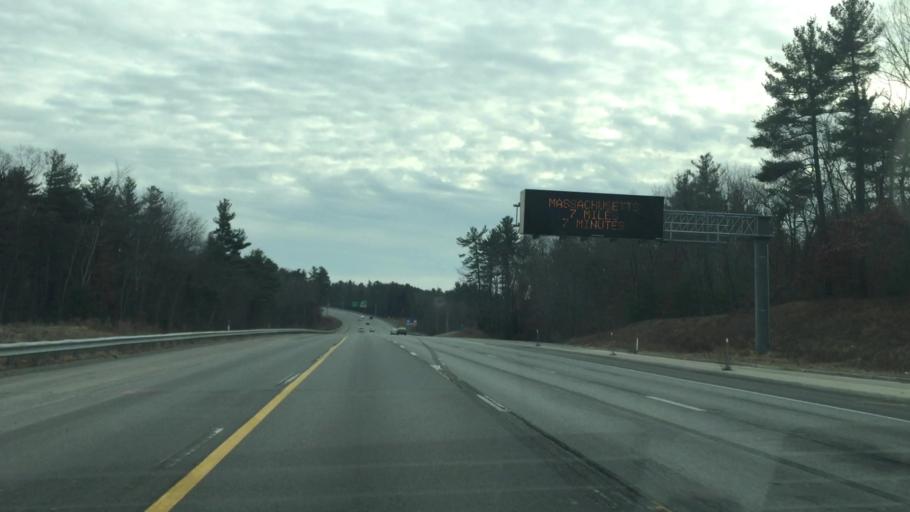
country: US
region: New Hampshire
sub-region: Rockingham County
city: Windham
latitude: 42.8219
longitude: -71.2893
